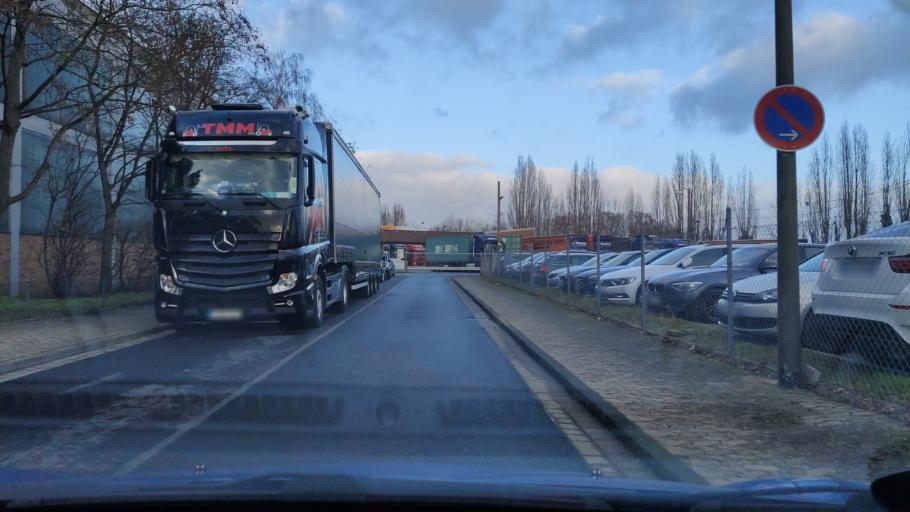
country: DE
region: Lower Saxony
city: Langenhagen
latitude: 52.4512
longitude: 9.7278
